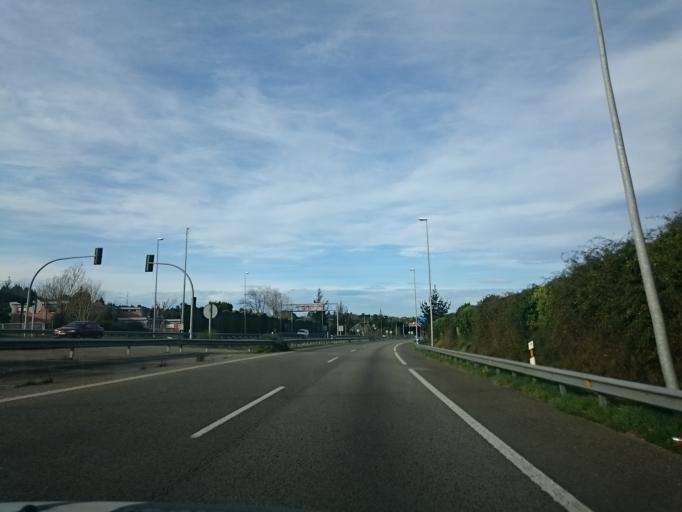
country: ES
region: Asturias
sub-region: Province of Asturias
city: Gijon
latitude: 43.5204
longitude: -5.6339
